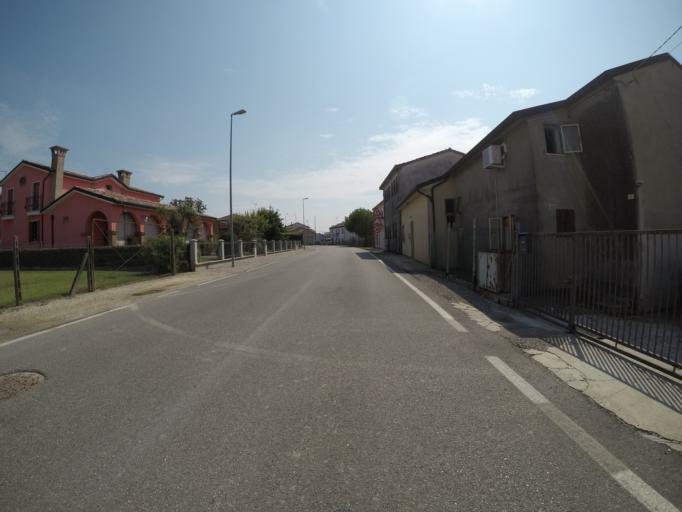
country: IT
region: Veneto
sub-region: Provincia di Rovigo
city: Lendinara
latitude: 45.1016
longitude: 11.5900
